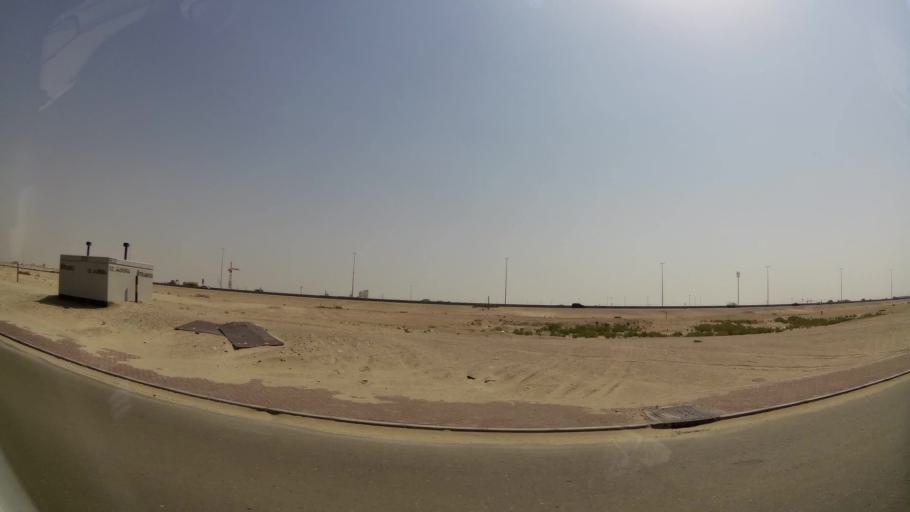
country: AE
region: Abu Dhabi
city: Abu Dhabi
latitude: 24.2990
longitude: 54.5797
